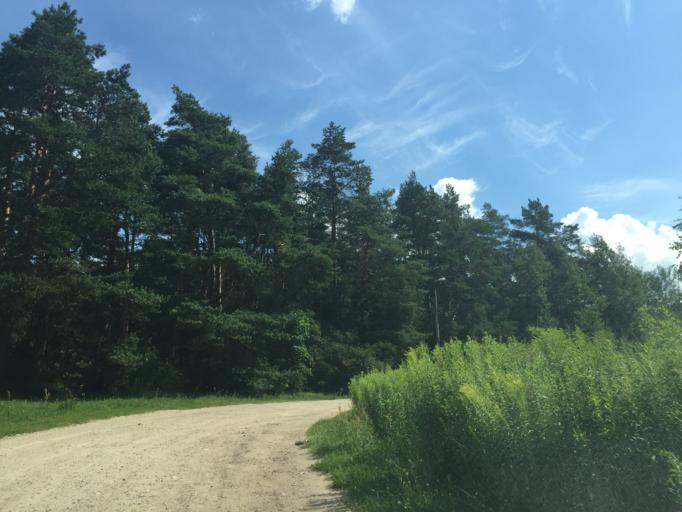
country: LV
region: Kekava
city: Balozi
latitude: 56.8912
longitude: 24.1448
